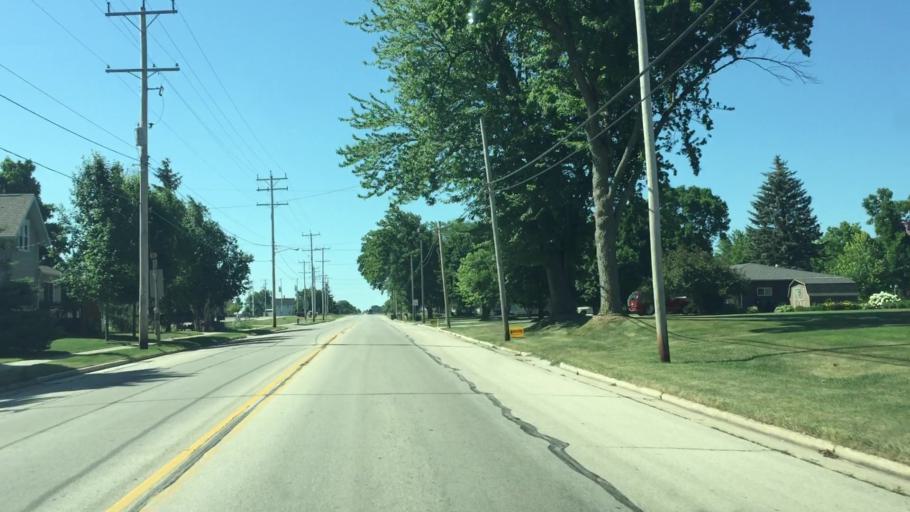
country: US
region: Wisconsin
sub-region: Calumet County
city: Hilbert
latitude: 44.1358
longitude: -88.1642
